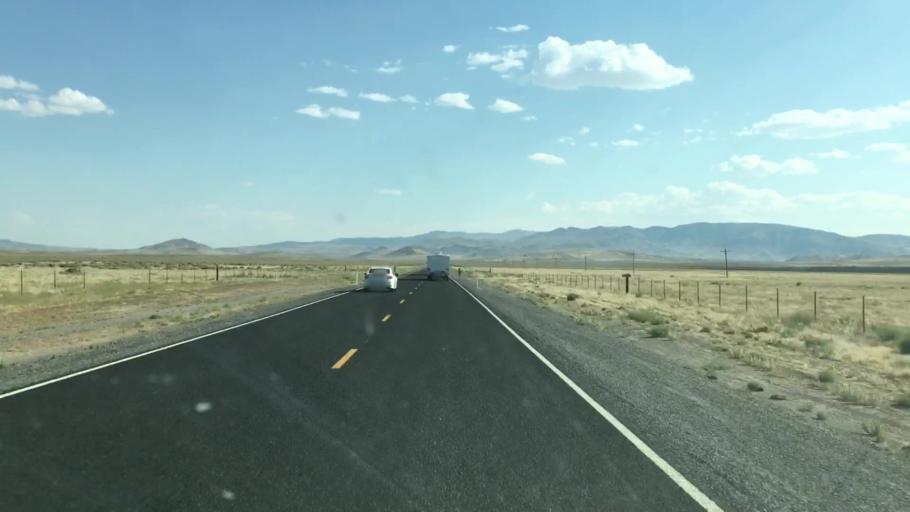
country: US
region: Nevada
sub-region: Lyon County
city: Fernley
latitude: 39.6809
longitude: -119.3346
